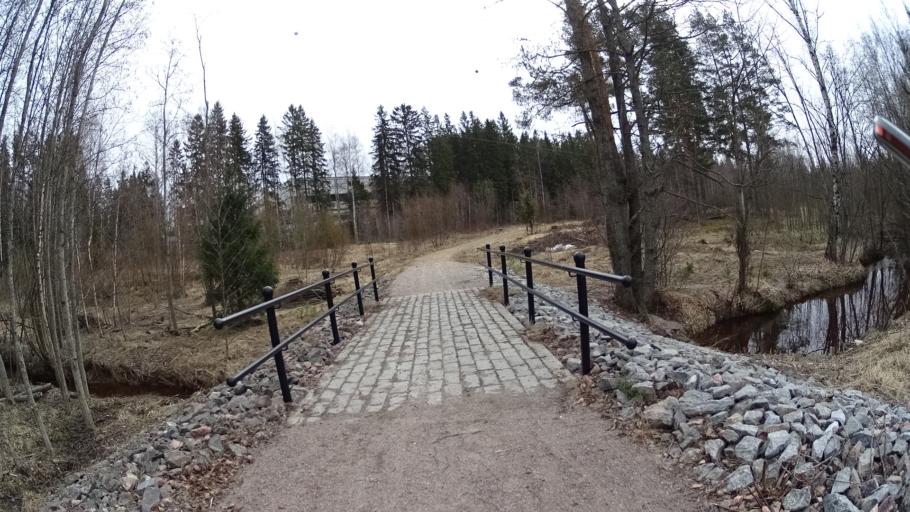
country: FI
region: Uusimaa
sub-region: Helsinki
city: Vantaa
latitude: 60.3002
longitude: 24.9372
